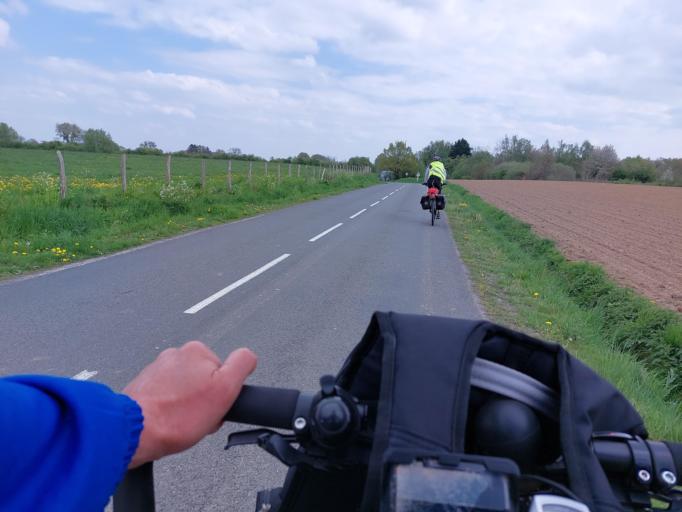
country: FR
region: Nord-Pas-de-Calais
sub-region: Departement du Nord
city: La Longueville
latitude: 50.2784
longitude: 3.8737
